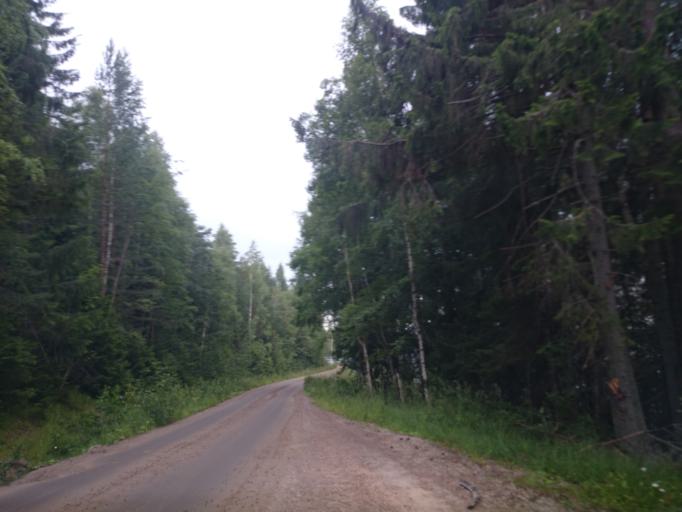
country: SE
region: Vaesternorrland
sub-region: Sundsvalls Kommun
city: Njurundabommen
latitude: 62.1358
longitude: 17.4150
